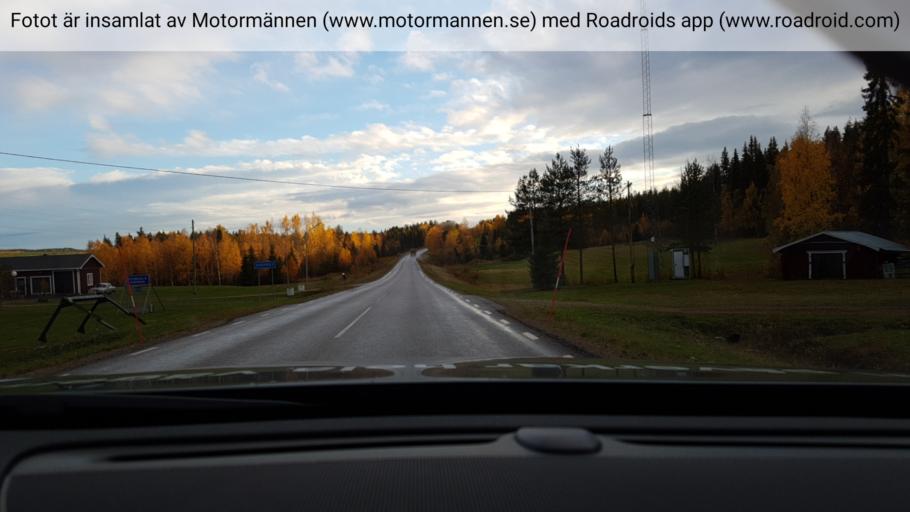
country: SE
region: Norrbotten
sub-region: Overkalix Kommun
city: OEverkalix
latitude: 66.7383
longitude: 22.6697
